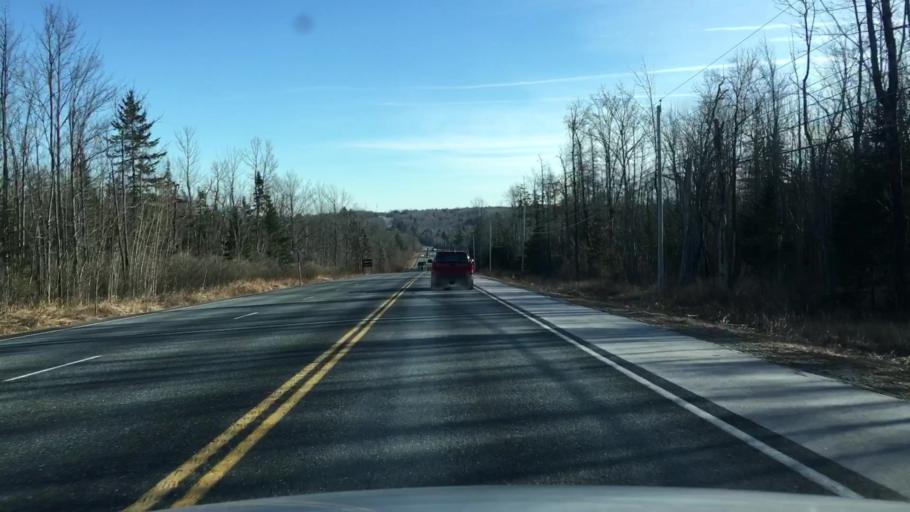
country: US
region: Maine
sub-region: Hancock County
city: Dedham
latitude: 44.6429
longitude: -68.5541
